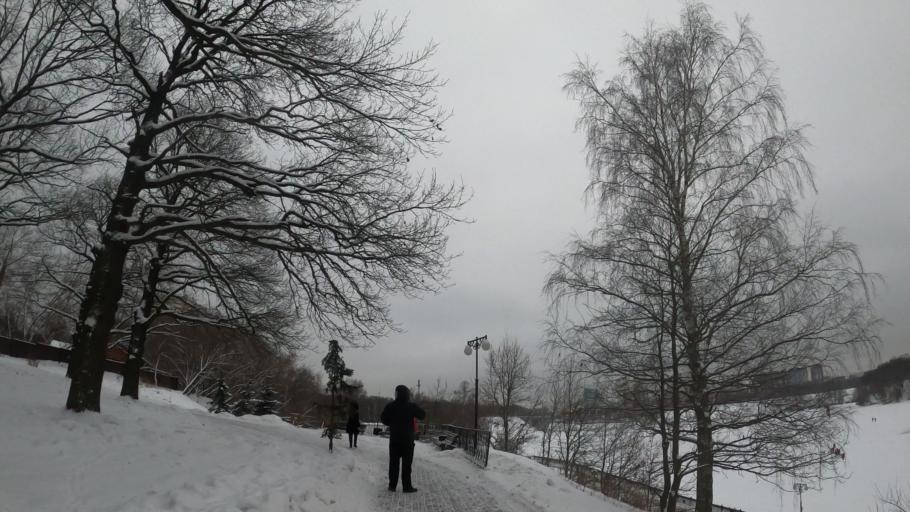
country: RU
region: Moskovskaya
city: Levoberezhnaya
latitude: 55.8933
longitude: 37.4684
